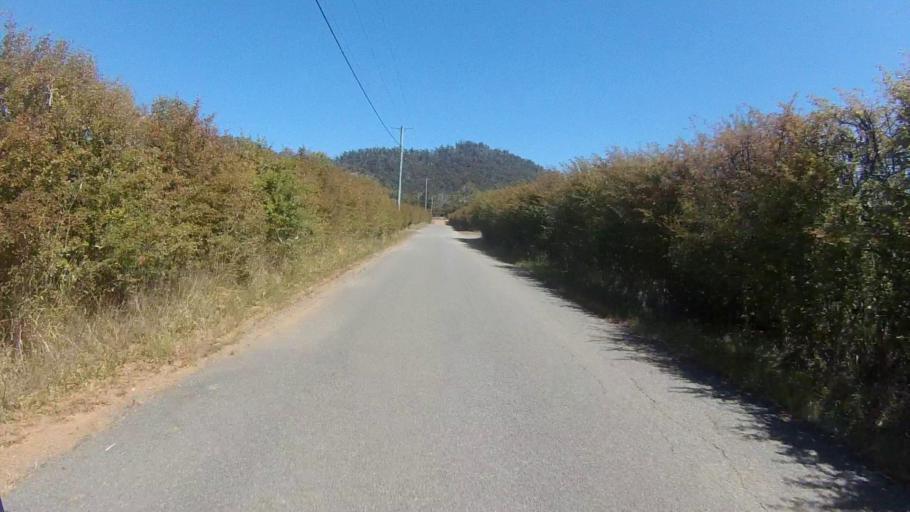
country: AU
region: Tasmania
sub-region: Clarence
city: Cambridge
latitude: -42.8451
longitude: 147.4583
